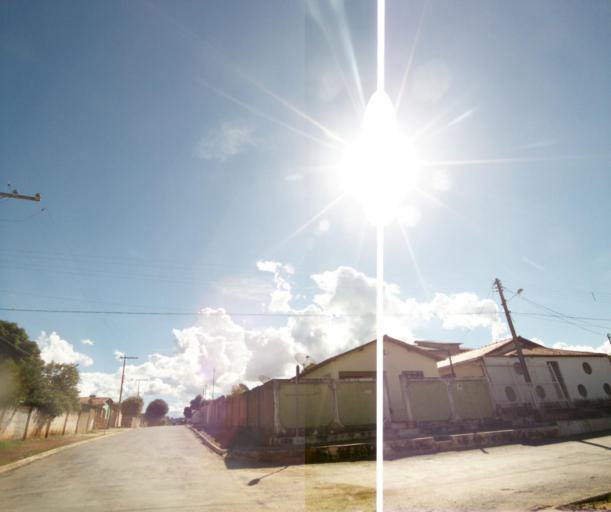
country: BR
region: Bahia
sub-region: Correntina
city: Correntina
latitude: -13.3466
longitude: -44.6382
